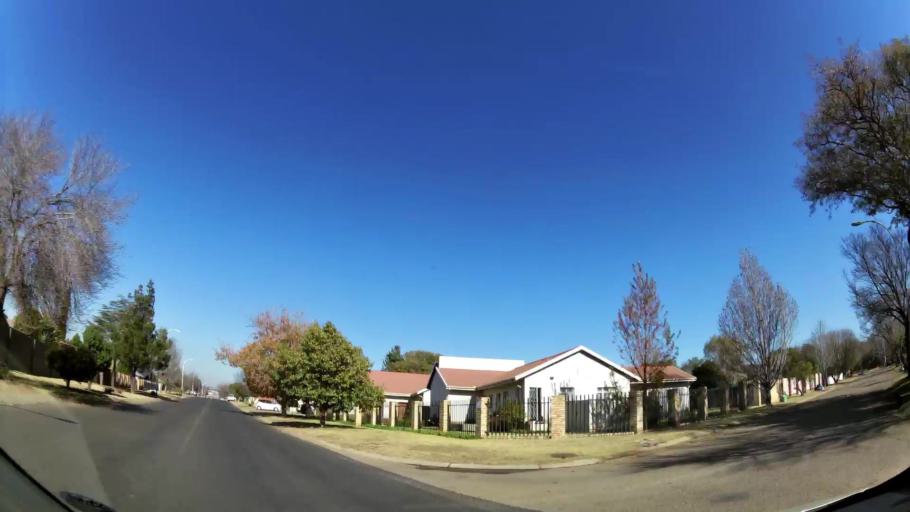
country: ZA
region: Mpumalanga
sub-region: Nkangala District Municipality
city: Witbank
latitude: -25.8733
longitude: 29.2506
